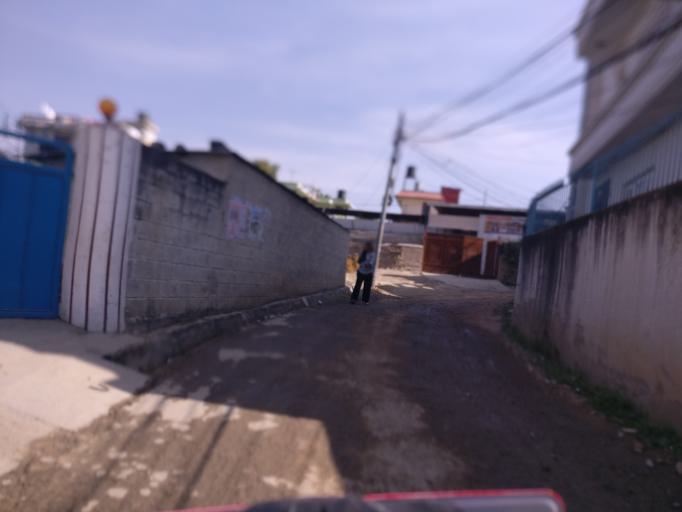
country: NP
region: Central Region
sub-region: Bagmati Zone
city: Patan
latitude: 27.6512
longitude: 85.3074
